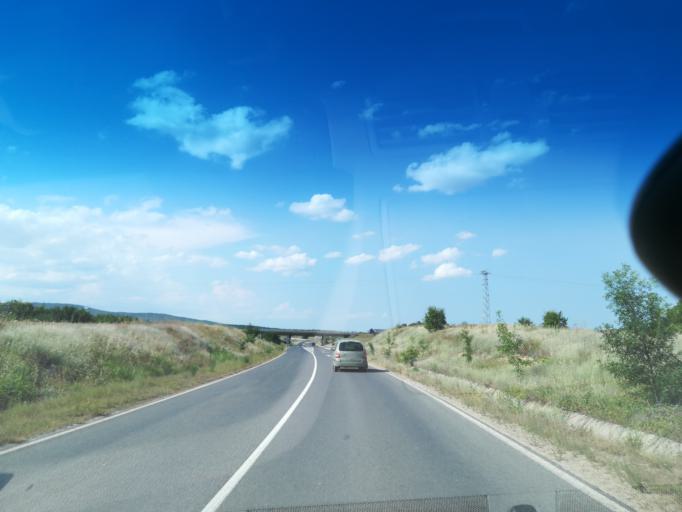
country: BG
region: Stara Zagora
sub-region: Obshtina Chirpan
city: Chirpan
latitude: 42.2479
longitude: 25.4121
